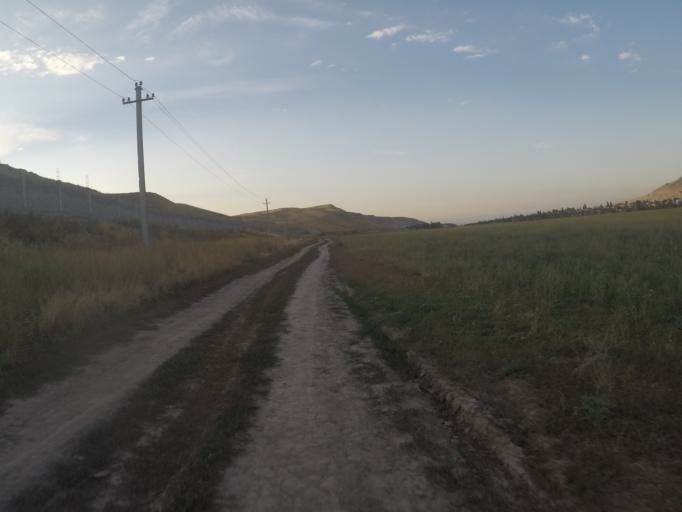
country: KG
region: Chuy
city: Bishkek
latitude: 42.7556
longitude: 74.6363
